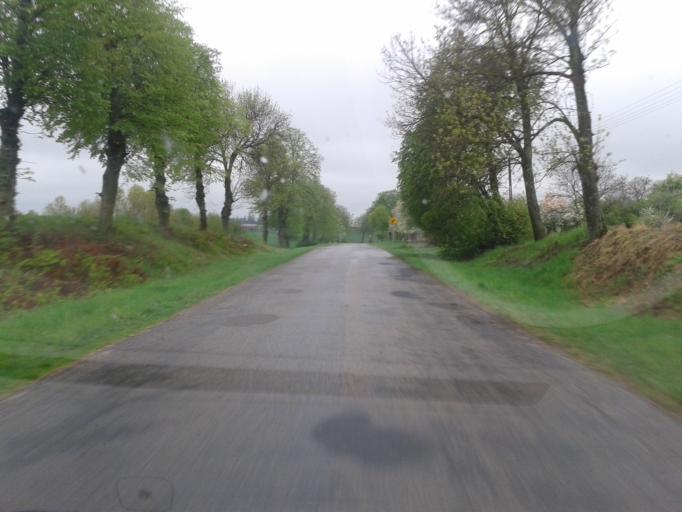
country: PL
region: Lublin Voivodeship
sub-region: Powiat tomaszowski
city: Telatyn
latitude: 50.4769
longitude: 23.8592
